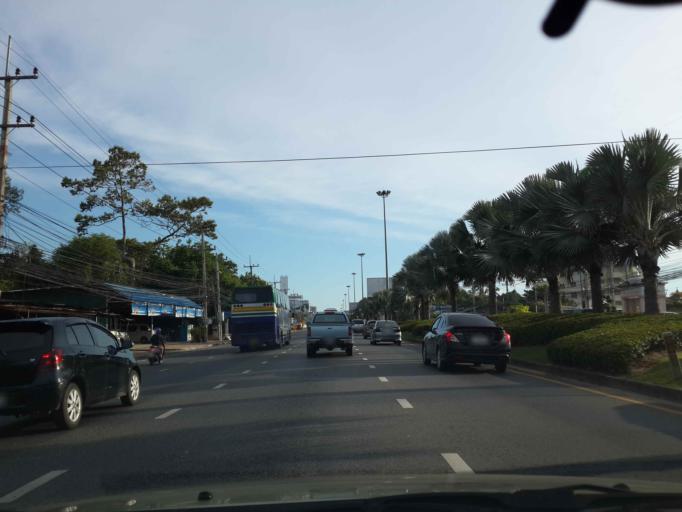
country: TH
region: Chon Buri
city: Phatthaya
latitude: 12.9820
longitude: 100.9194
